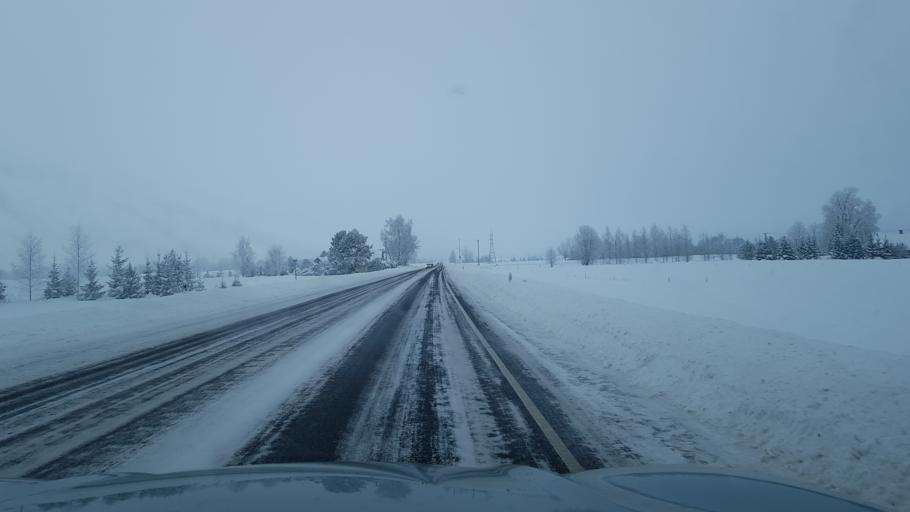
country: EE
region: Ida-Virumaa
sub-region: Johvi vald
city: Johvi
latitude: 59.2356
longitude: 27.3477
